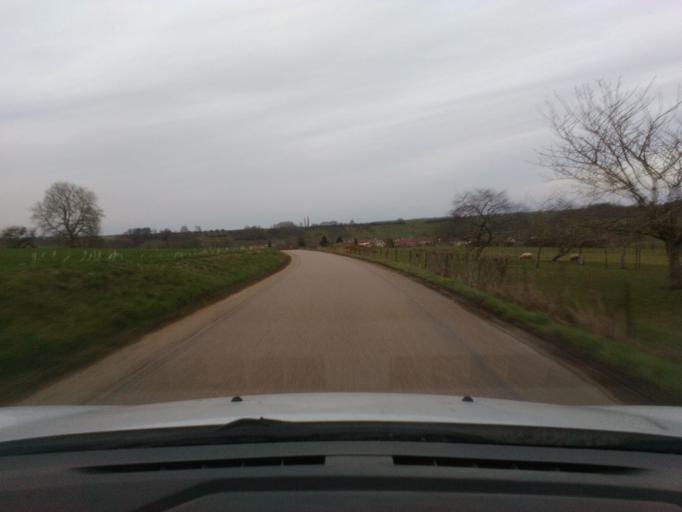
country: FR
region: Lorraine
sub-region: Departement des Vosges
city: Mirecourt
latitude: 48.3045
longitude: 6.0978
